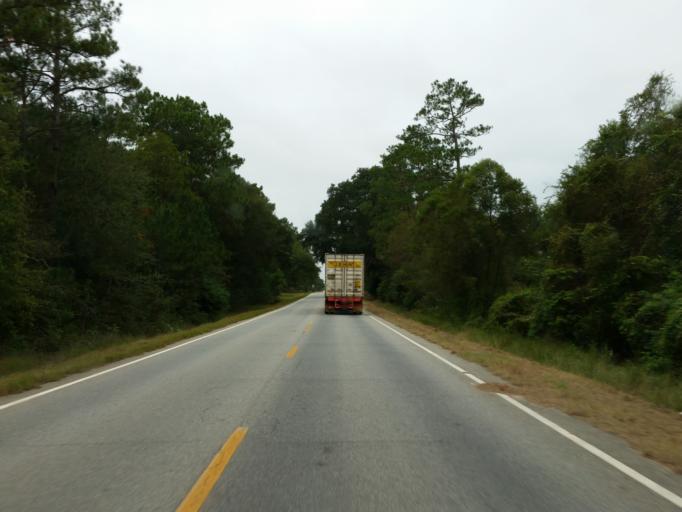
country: US
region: Georgia
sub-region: Berrien County
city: Ray City
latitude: 31.0844
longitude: -83.2353
